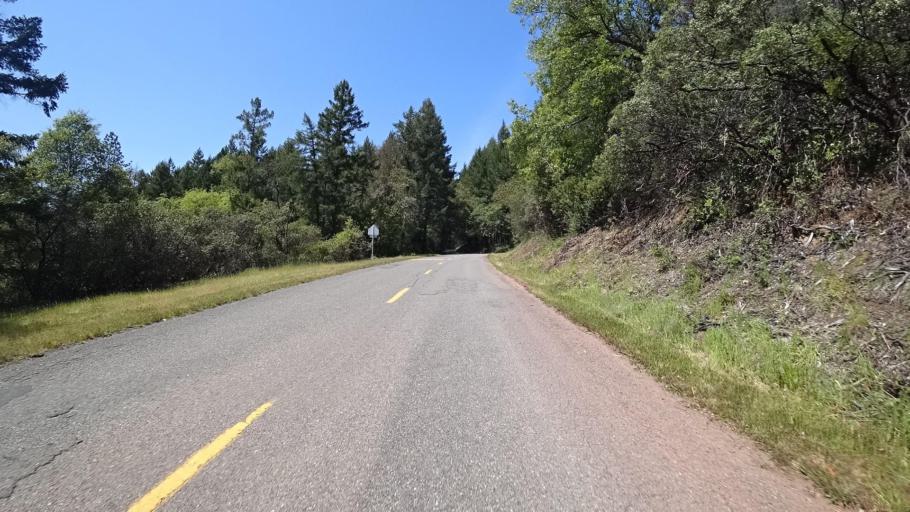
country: US
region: California
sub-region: Humboldt County
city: Redway
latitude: 40.2426
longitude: -123.6249
